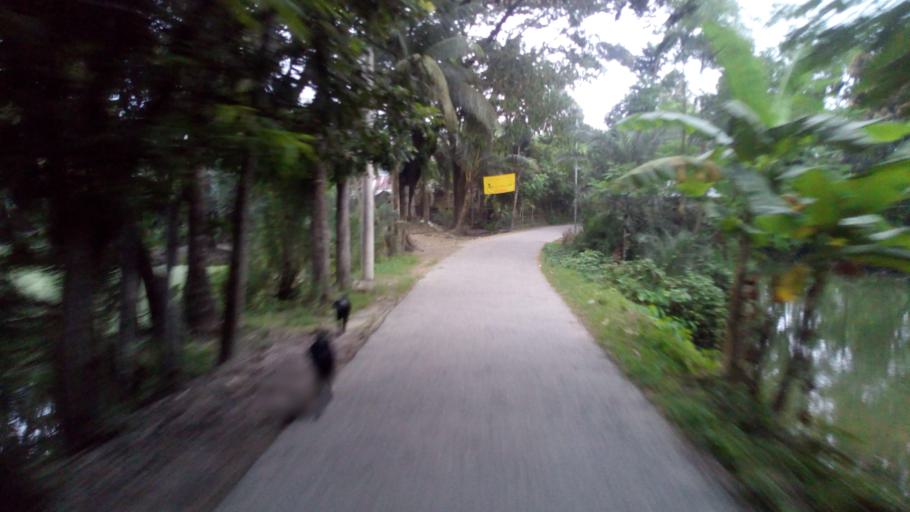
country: BD
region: Khulna
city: Phultala
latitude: 22.7598
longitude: 89.4078
